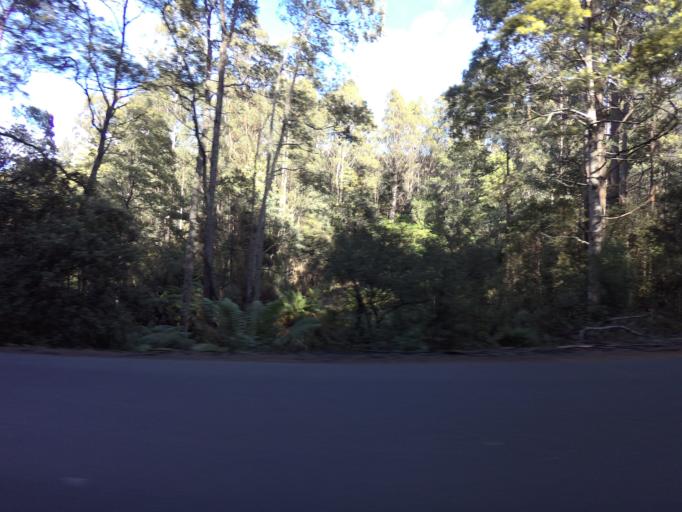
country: AU
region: Tasmania
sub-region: Huon Valley
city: Cygnet
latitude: -43.2632
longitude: 147.0090
